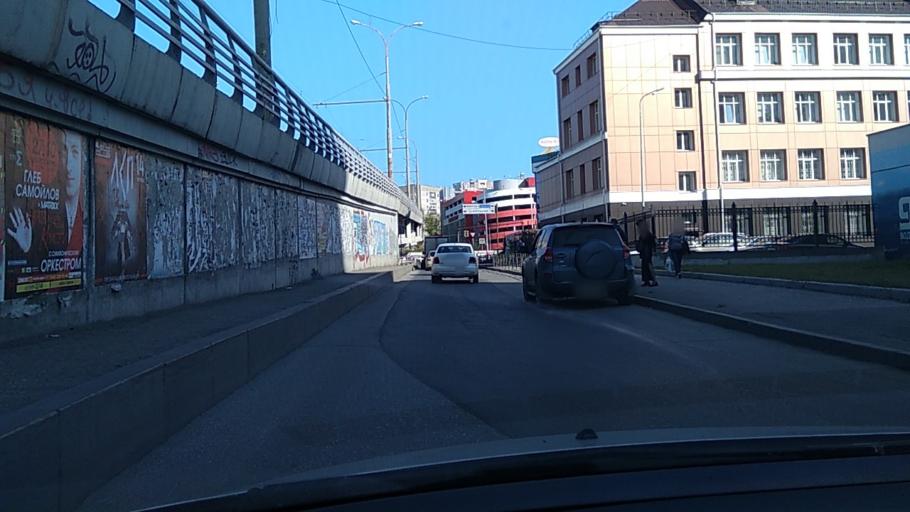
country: RU
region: Sverdlovsk
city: Yekaterinburg
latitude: 56.8492
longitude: 60.6229
